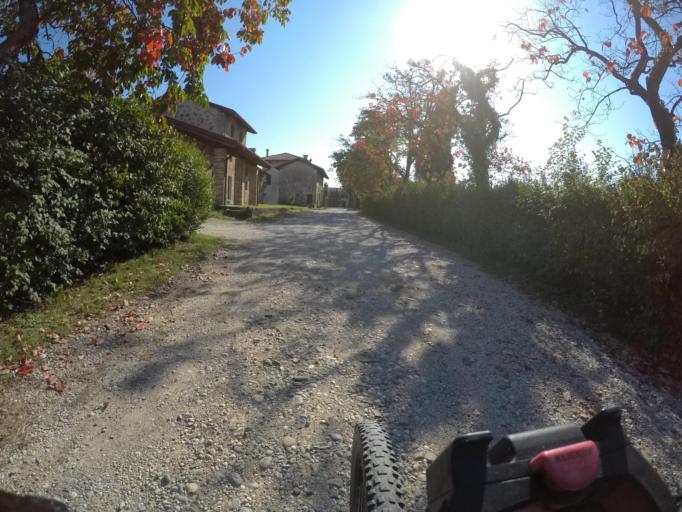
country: IT
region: Friuli Venezia Giulia
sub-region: Provincia di Udine
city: Manzano
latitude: 46.0104
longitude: 13.3638
